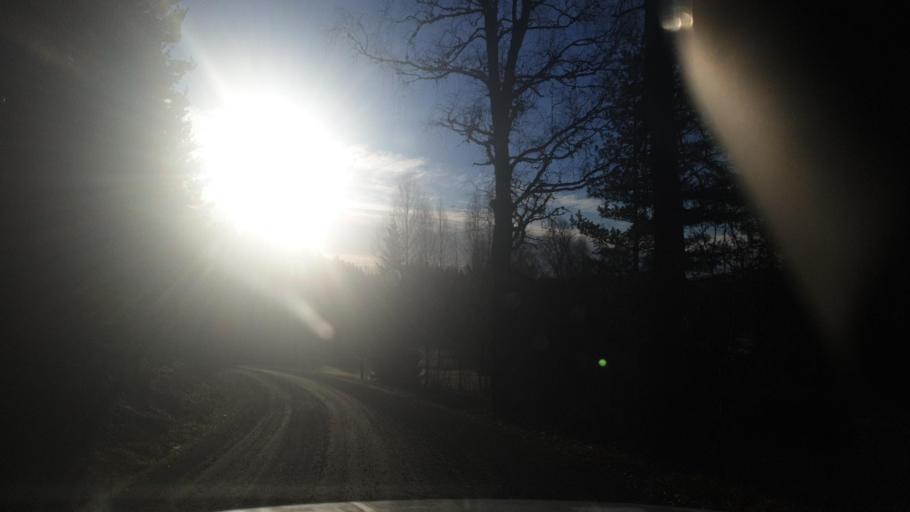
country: SE
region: Vaermland
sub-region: Sunne Kommun
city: Sunne
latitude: 59.6403
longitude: 13.0598
